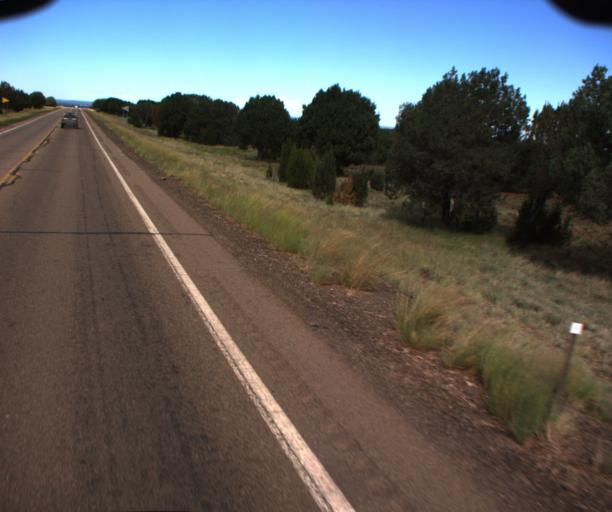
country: US
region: Arizona
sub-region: Navajo County
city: White Mountain Lake
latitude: 34.2757
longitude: -109.8956
